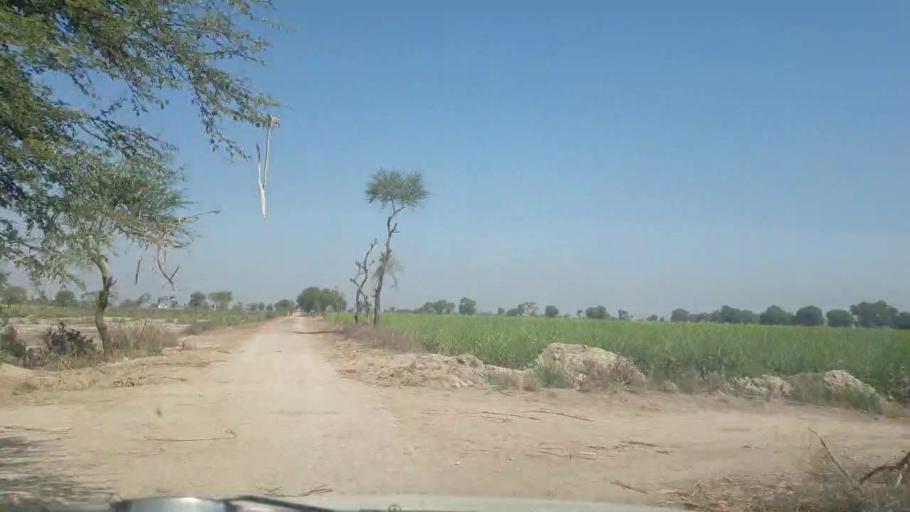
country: PK
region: Sindh
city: Mirpur Khas
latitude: 25.5482
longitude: 69.1965
